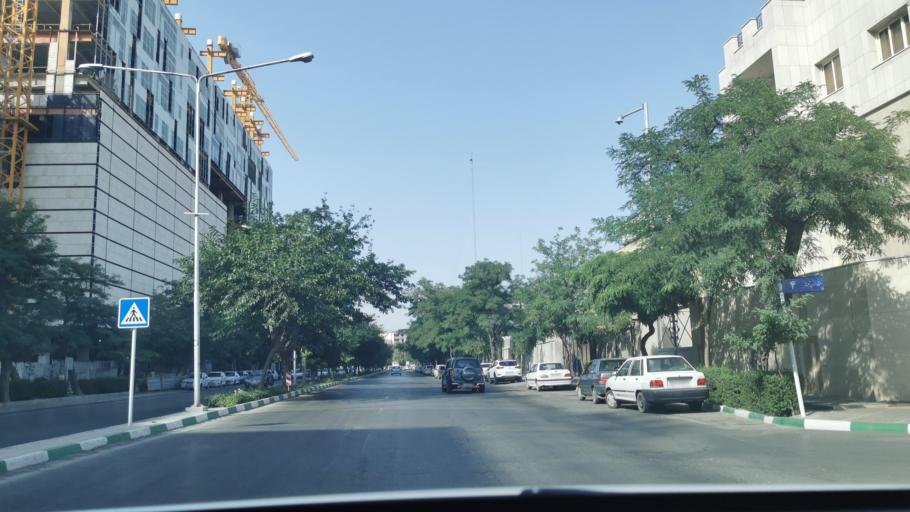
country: IR
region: Razavi Khorasan
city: Mashhad
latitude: 36.3184
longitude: 59.5608
